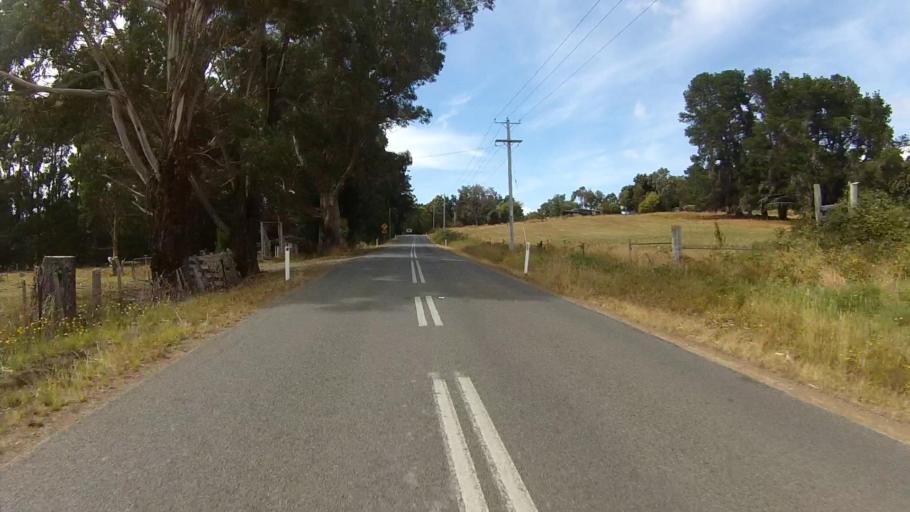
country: AU
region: Tasmania
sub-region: Kingborough
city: Kettering
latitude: -43.1830
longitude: 147.2402
